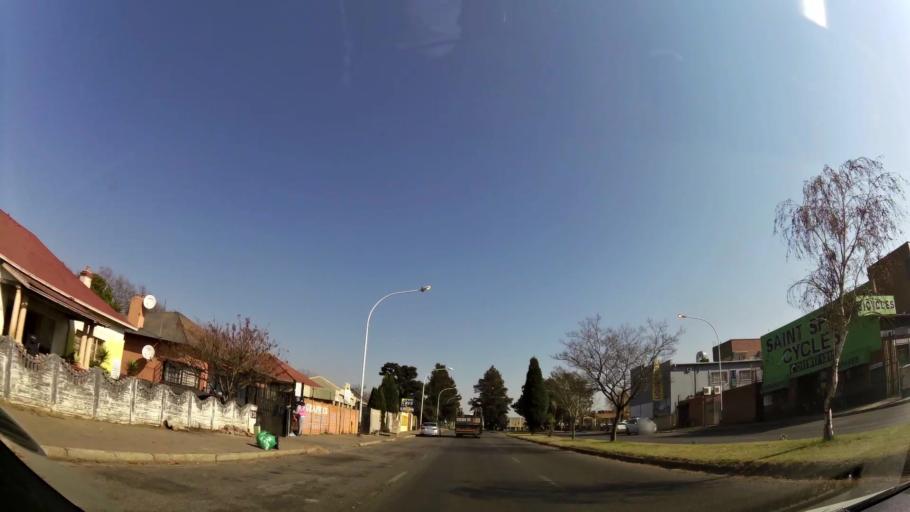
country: ZA
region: Gauteng
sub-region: Ekurhuleni Metropolitan Municipality
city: Boksburg
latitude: -26.2243
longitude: 28.2572
